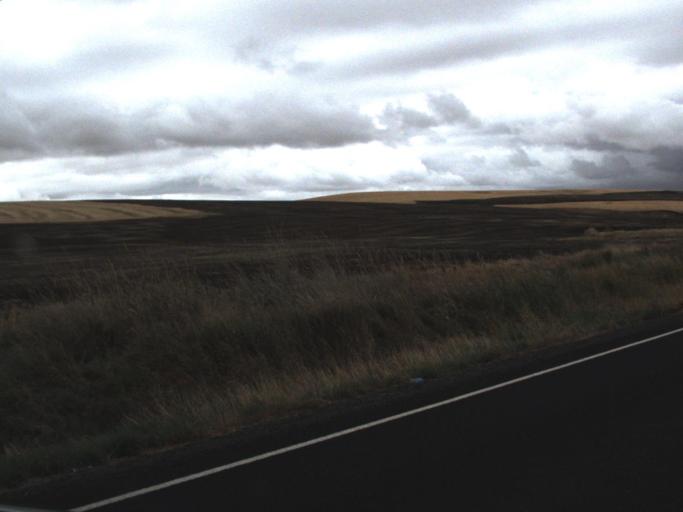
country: US
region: Washington
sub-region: Whitman County
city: Colfax
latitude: 47.2006
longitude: -117.3497
